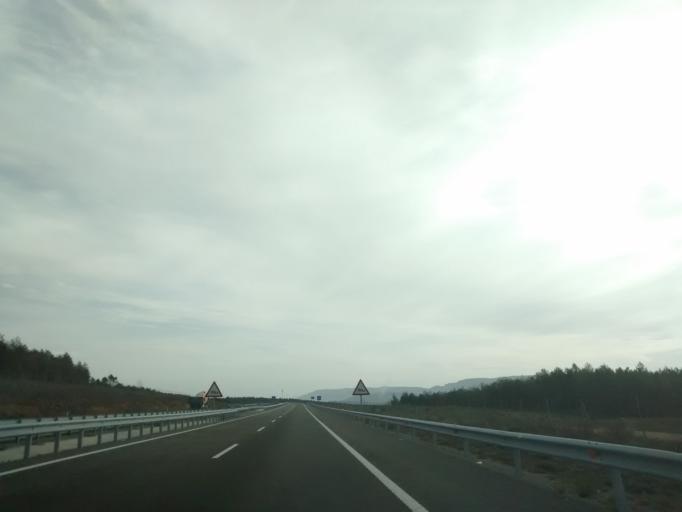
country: ES
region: Navarre
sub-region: Provincia de Navarra
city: Yesa
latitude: 42.6201
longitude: -1.1515
